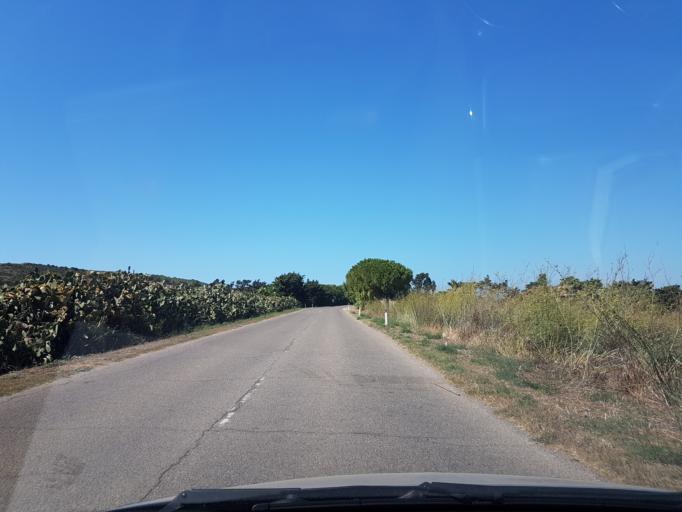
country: IT
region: Sardinia
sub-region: Provincia di Oristano
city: Cabras
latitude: 39.9420
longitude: 8.4574
